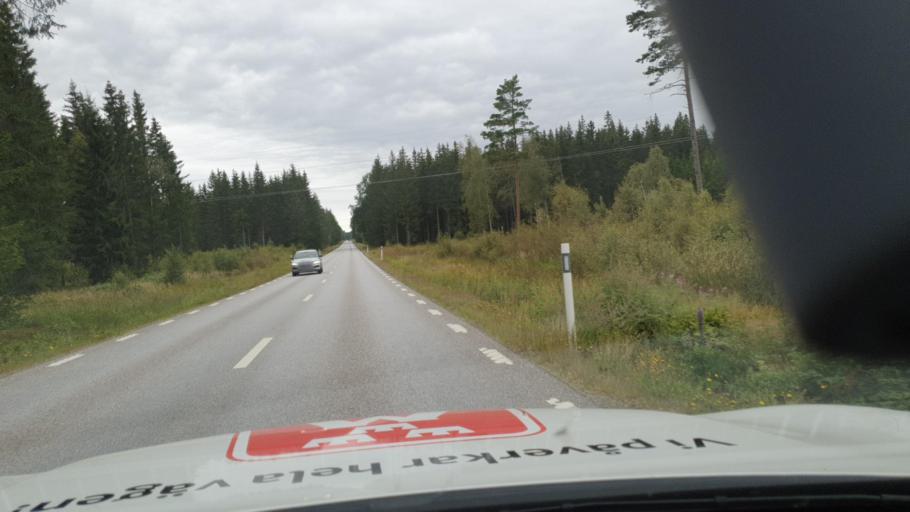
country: SE
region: Vaestra Goetaland
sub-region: Dals-Ed Kommun
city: Ed
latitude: 58.8839
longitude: 11.9830
